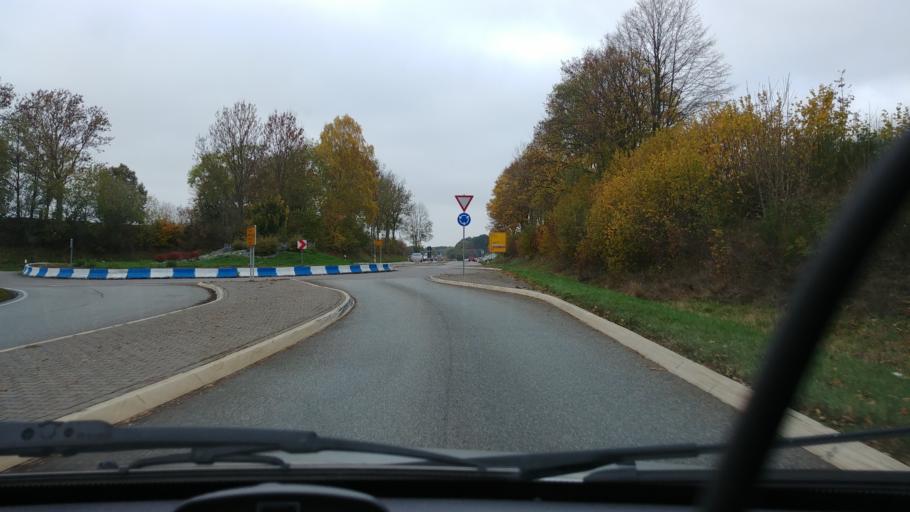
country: DE
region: Rheinland-Pfalz
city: Muschenbach
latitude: 50.6720
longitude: 7.8030
